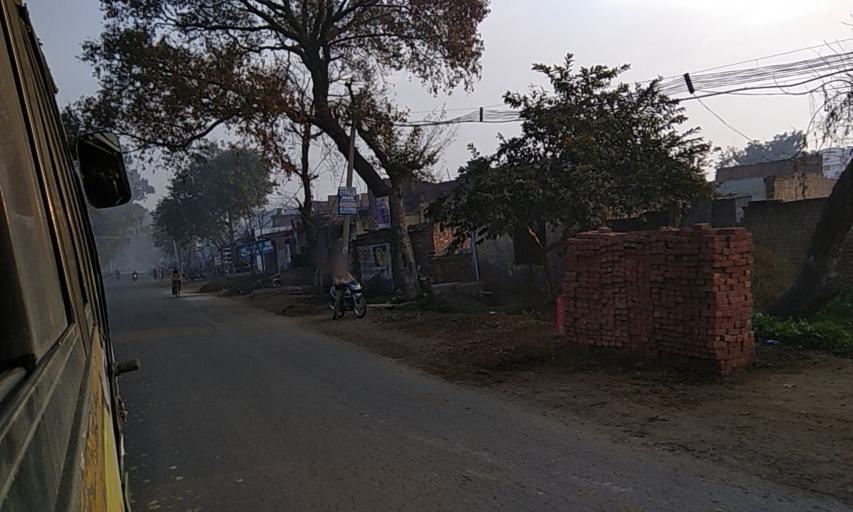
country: IN
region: Punjab
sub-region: Gurdaspur
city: Dhariwal
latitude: 31.9299
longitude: 75.3041
